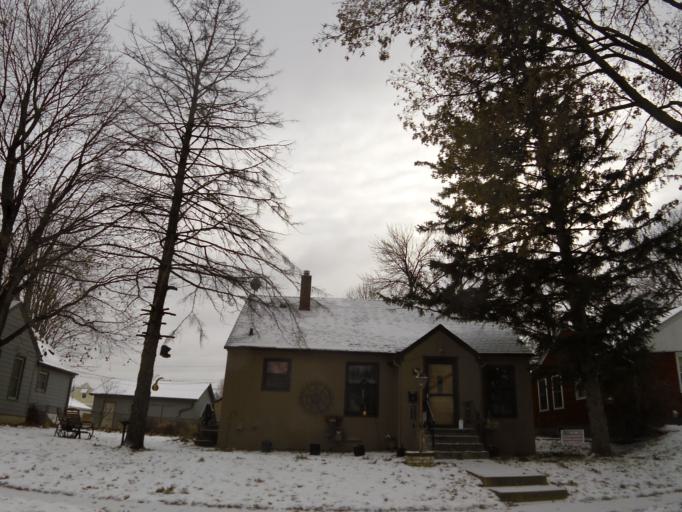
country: US
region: Minnesota
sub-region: Dakota County
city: Mendota Heights
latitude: 44.9224
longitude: -93.1408
